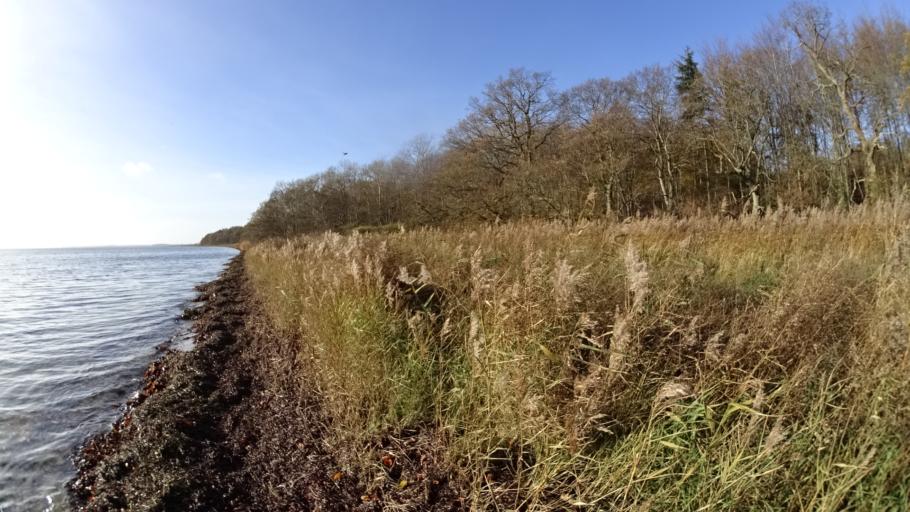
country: DK
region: Central Jutland
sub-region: Odder Kommune
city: Odder
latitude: 55.9082
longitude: 10.2390
